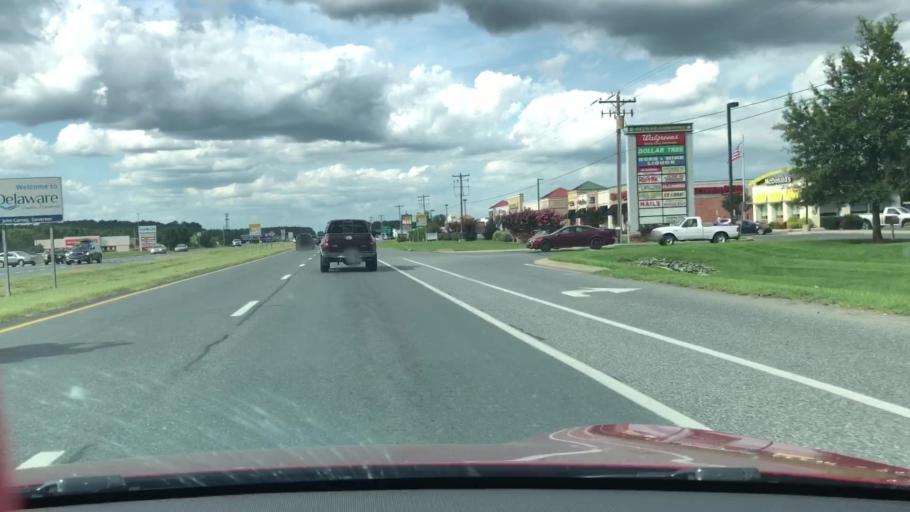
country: US
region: Delaware
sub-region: Sussex County
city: Delmar
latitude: 38.4563
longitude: -75.5581
